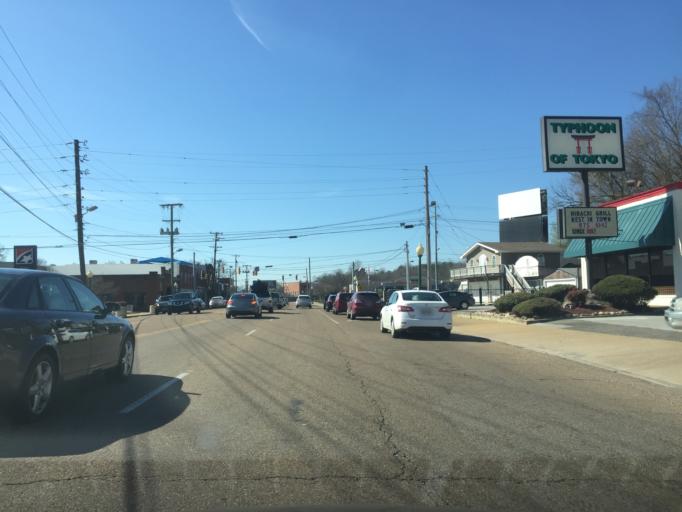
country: US
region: Tennessee
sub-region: Hamilton County
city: Red Bank
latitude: 35.1206
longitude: -85.2889
